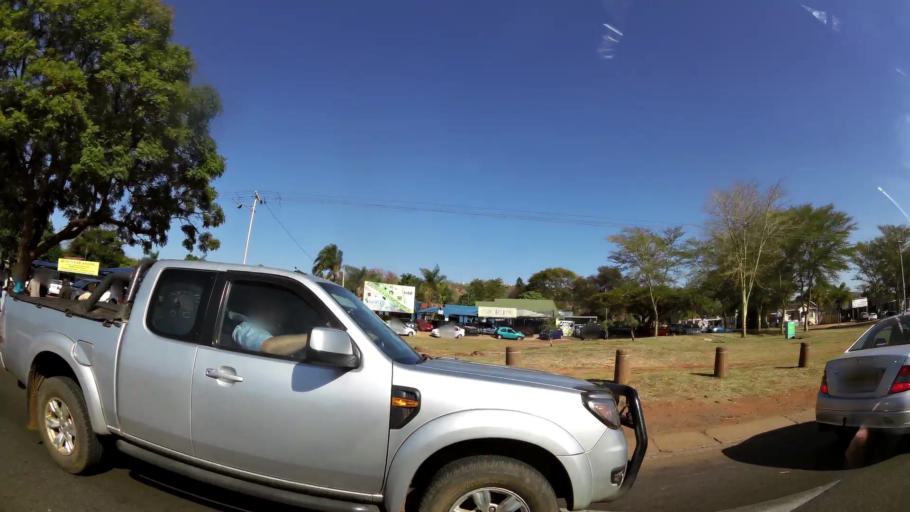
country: ZA
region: Gauteng
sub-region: City of Tshwane Metropolitan Municipality
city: Pretoria
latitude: -25.6806
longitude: 28.2168
